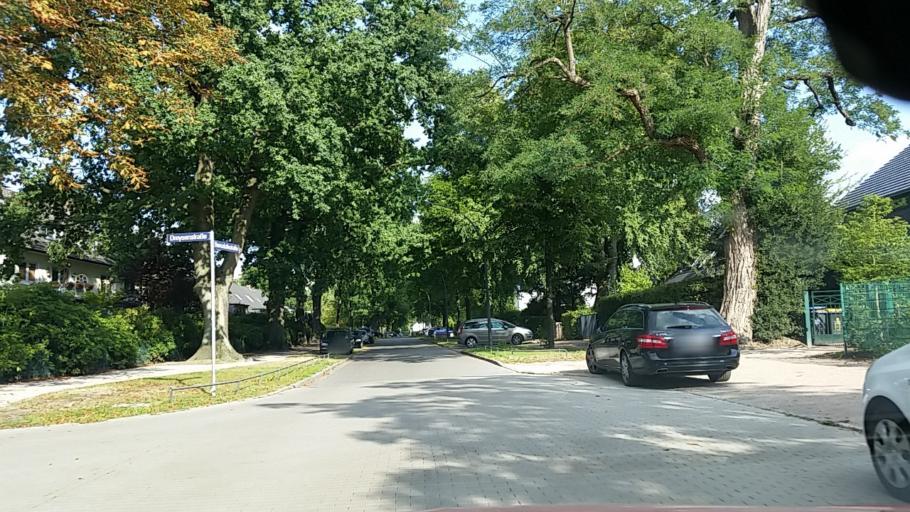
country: DE
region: Hamburg
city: Altona
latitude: 53.5482
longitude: 9.8852
